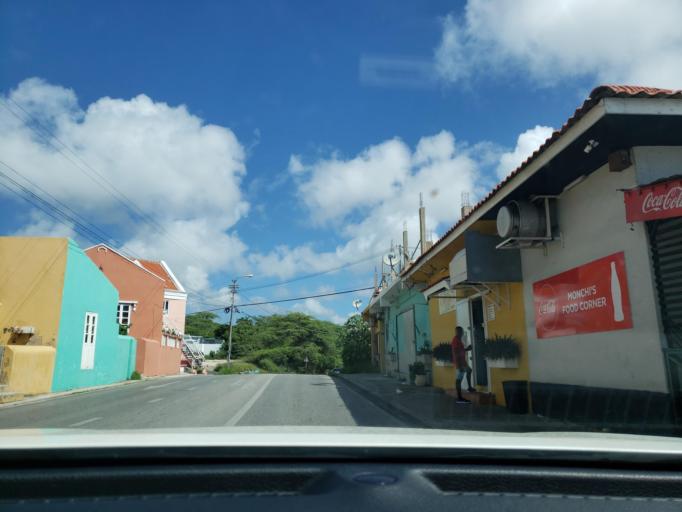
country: CW
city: Willemstad
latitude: 12.1041
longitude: -68.9185
